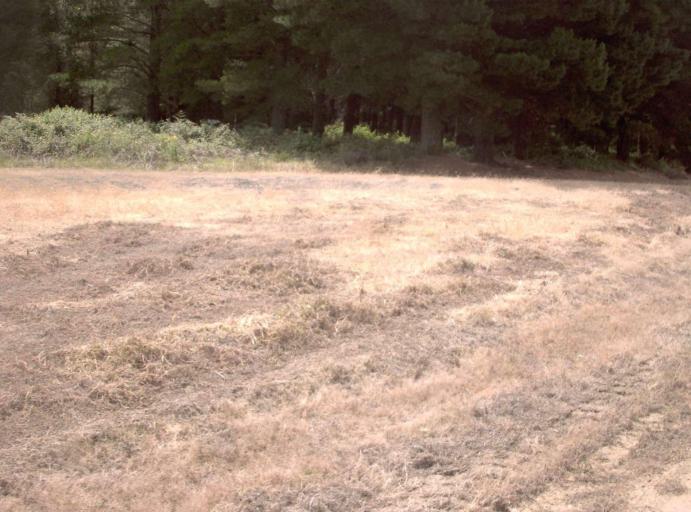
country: AU
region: Victoria
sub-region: Latrobe
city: Traralgon
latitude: -38.3937
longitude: 146.6594
